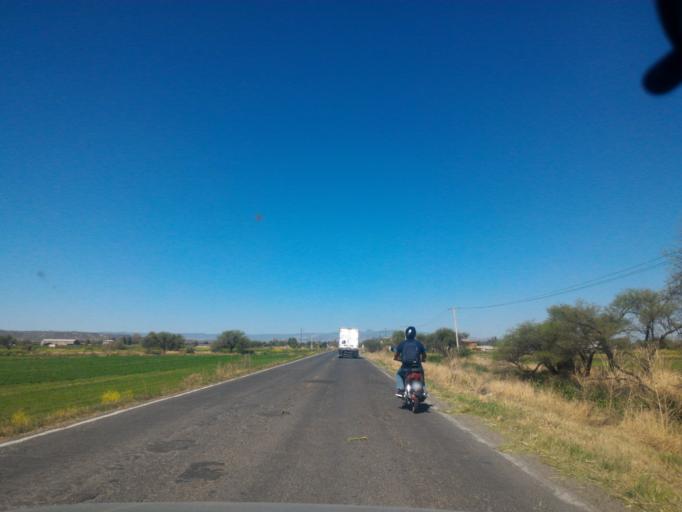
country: MX
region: Guanajuato
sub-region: San Francisco del Rincon
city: San Roque de Montes
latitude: 21.0135
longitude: -101.7986
